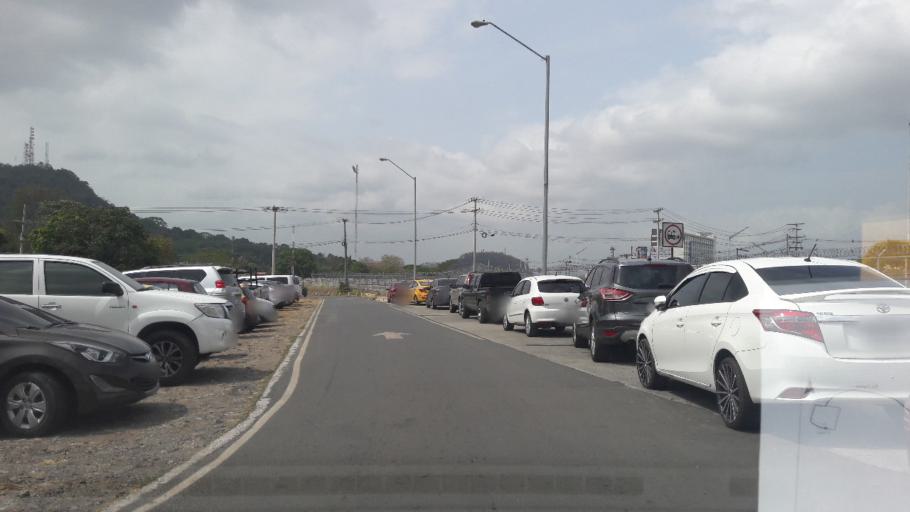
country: PA
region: Panama
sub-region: Distrito de Panama
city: Ancon
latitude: 8.9727
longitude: -79.5495
